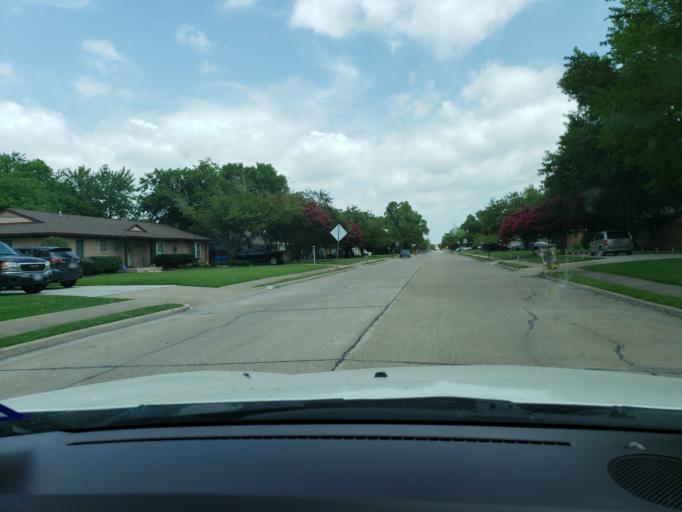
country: US
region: Texas
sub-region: Dallas County
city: Rowlett
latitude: 32.8962
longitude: -96.5630
